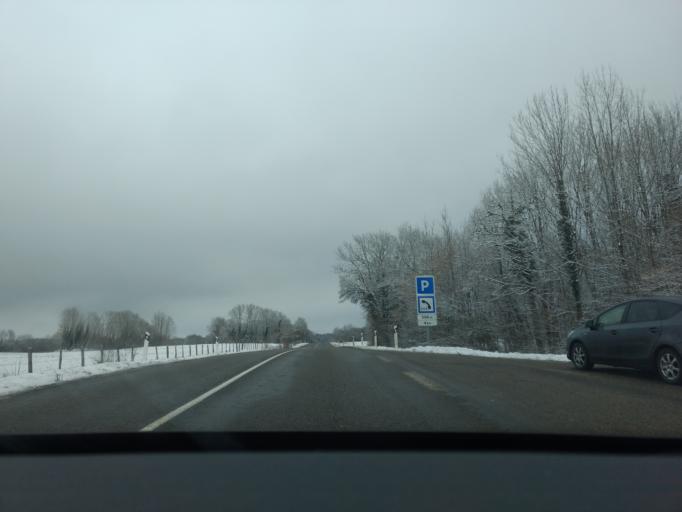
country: FR
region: Franche-Comte
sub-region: Departement du Jura
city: Champagnole
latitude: 46.7901
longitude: 5.8457
